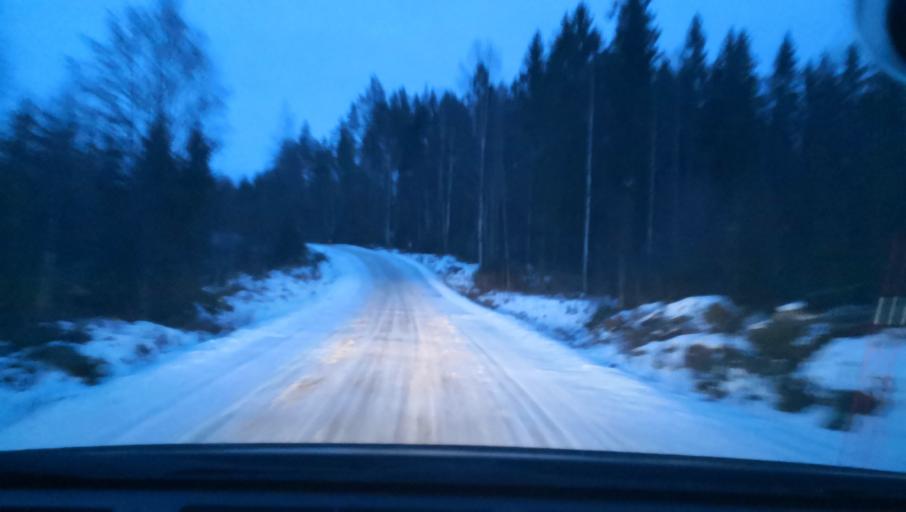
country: SE
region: Dalarna
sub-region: Avesta Kommun
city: Horndal
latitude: 60.2280
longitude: 16.6437
